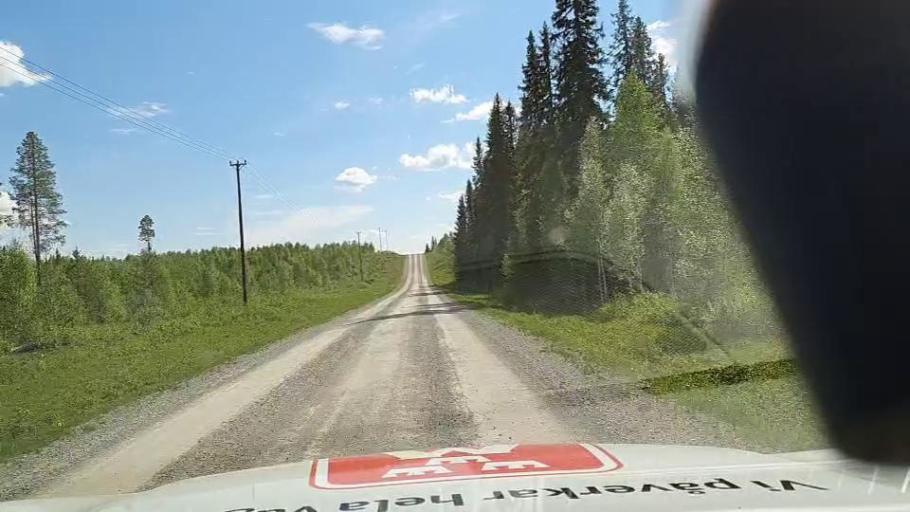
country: SE
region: Jaemtland
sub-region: Stroemsunds Kommun
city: Stroemsund
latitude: 64.4886
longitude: 15.5911
